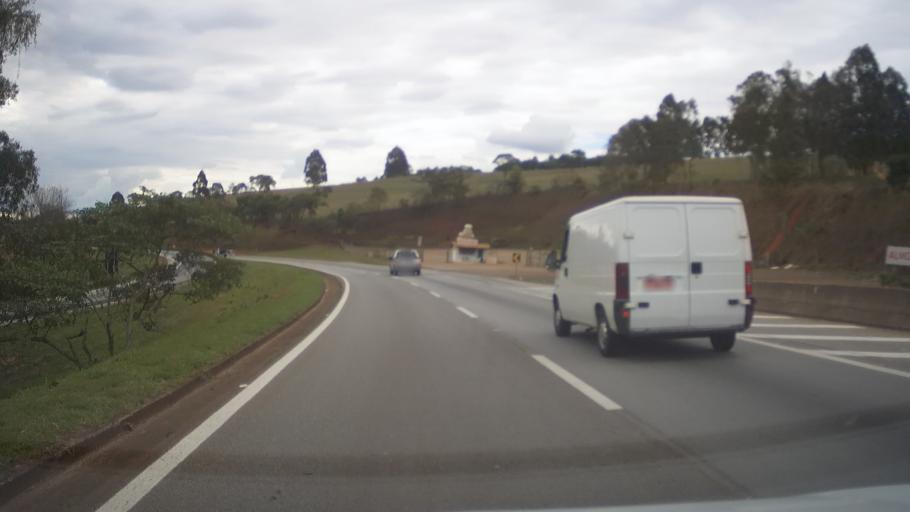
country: BR
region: Minas Gerais
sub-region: Itauna
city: Itauna
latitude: -20.3393
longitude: -44.4415
